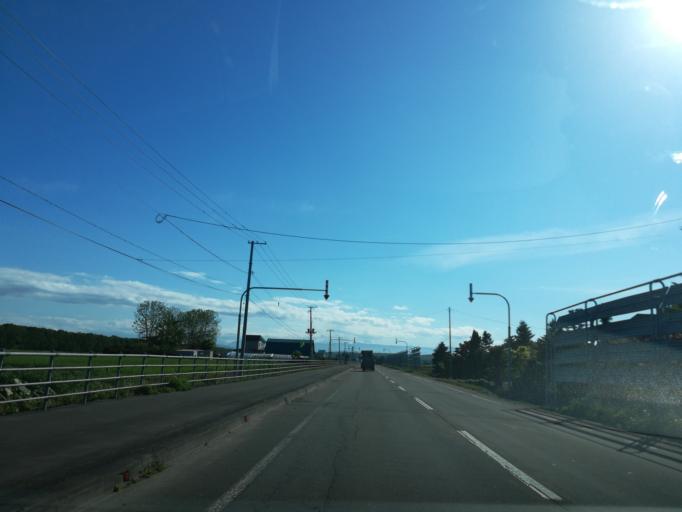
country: JP
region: Hokkaido
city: Kitahiroshima
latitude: 43.0446
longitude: 141.5921
